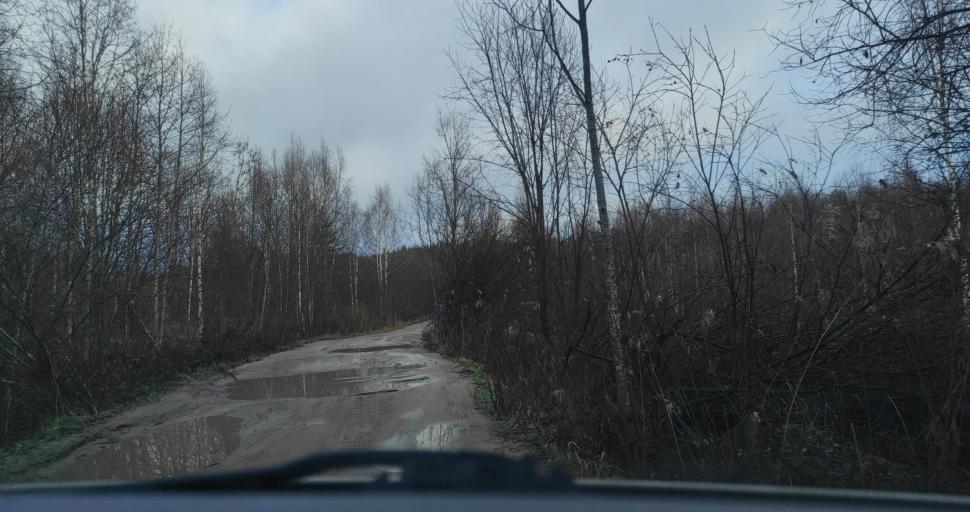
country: RU
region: Republic of Karelia
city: Pitkyaranta
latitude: 61.7332
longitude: 31.3859
